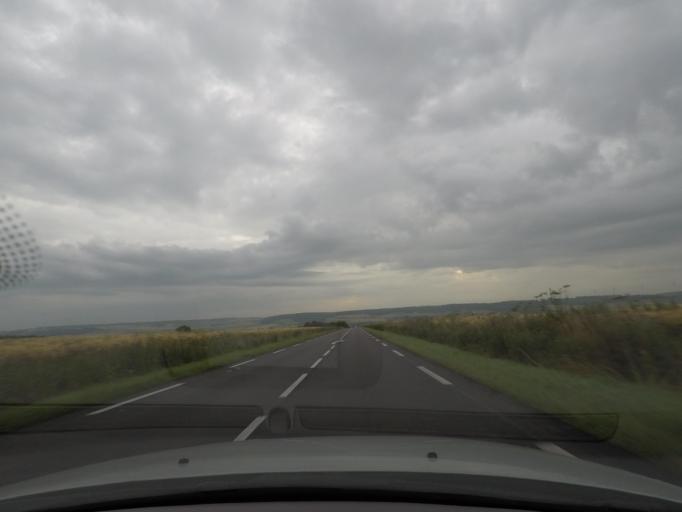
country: FR
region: Haute-Normandie
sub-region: Departement de la Seine-Maritime
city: Neufchatel-en-Bray
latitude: 49.7396
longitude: 1.5220
